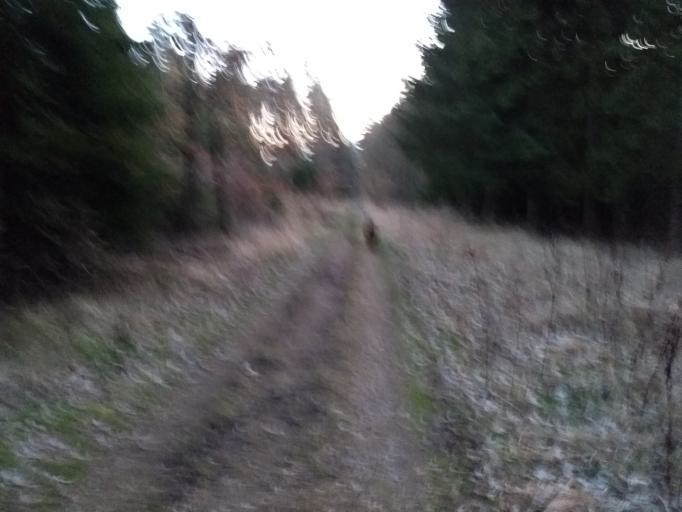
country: CZ
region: Central Bohemia
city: Unhost'
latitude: 50.0436
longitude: 14.1485
